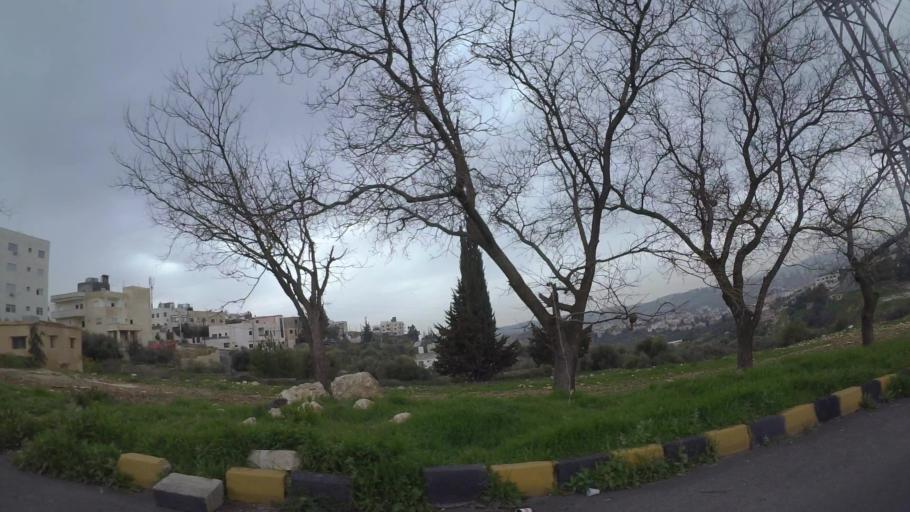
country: JO
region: Amman
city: Umm as Summaq
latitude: 31.9089
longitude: 35.8363
